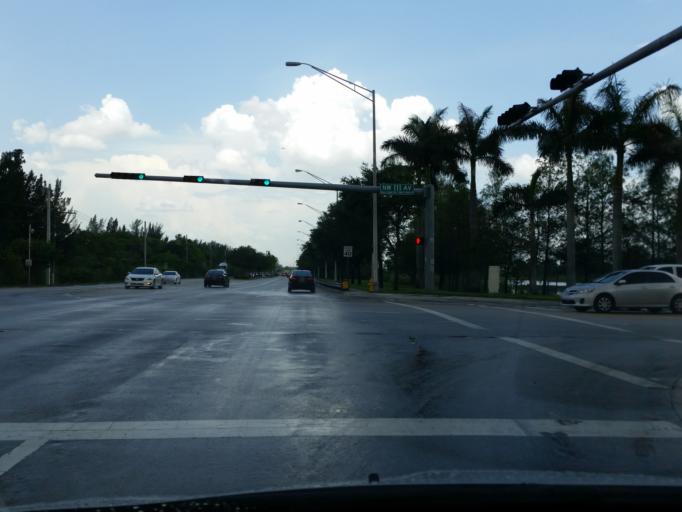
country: US
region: Florida
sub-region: Miami-Dade County
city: Sweetwater
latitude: 25.7828
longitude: -80.3749
